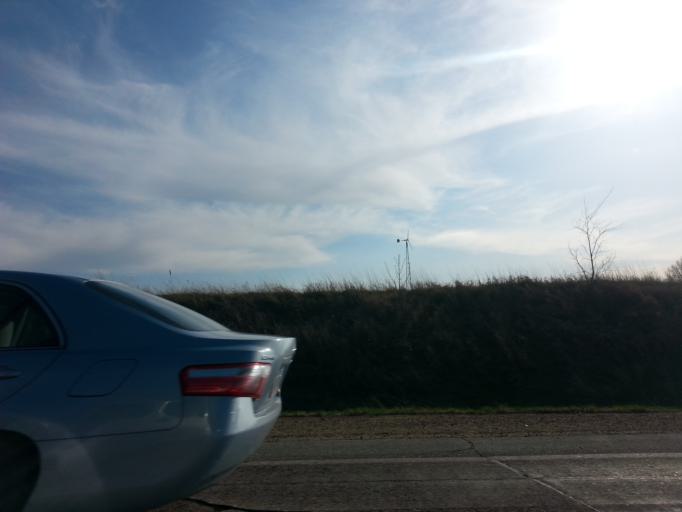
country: US
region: Wisconsin
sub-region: Pierce County
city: River Falls
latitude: 44.7409
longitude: -92.6383
